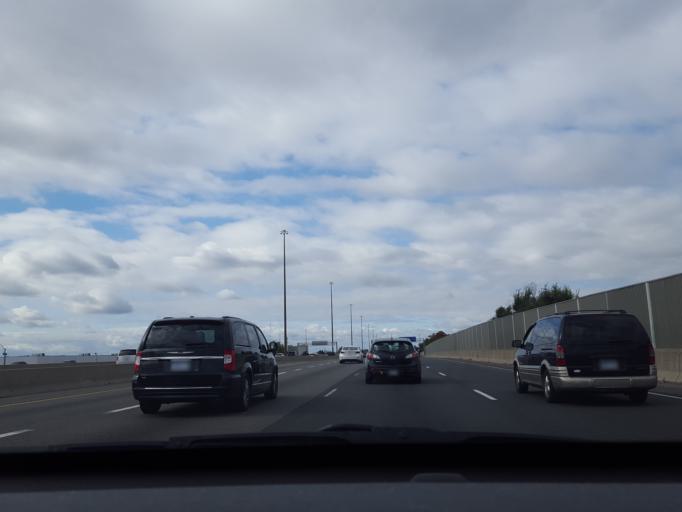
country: CA
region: Ontario
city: Scarborough
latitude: 43.7733
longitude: -79.2929
